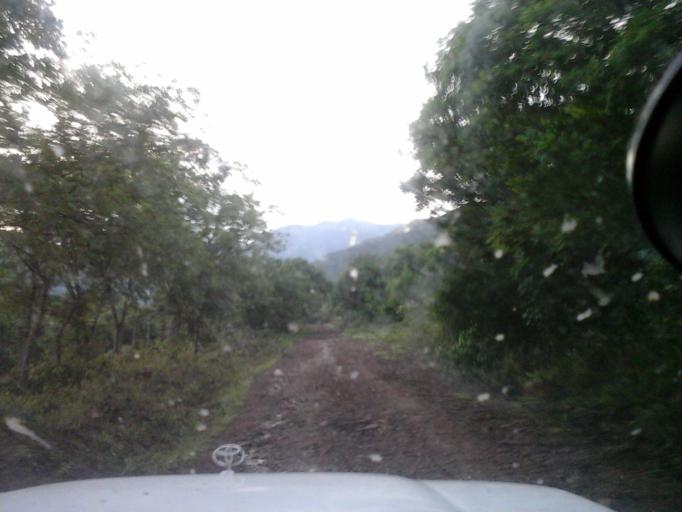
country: CO
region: Cesar
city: Agustin Codazzi
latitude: 10.1717
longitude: -73.1660
